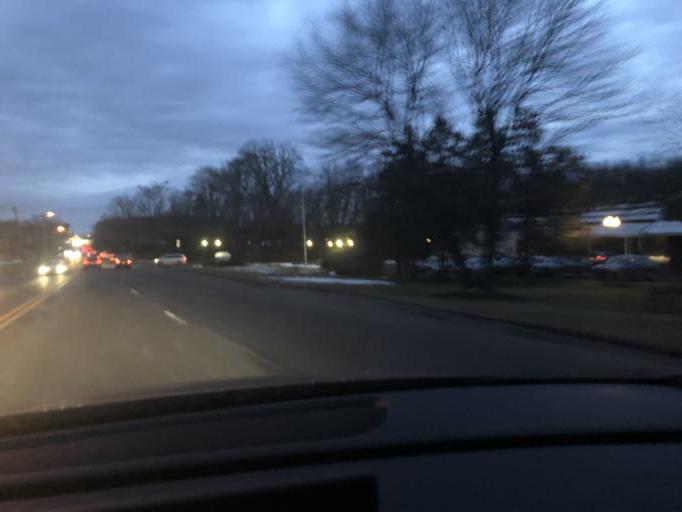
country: US
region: New Jersey
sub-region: Morris County
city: Florham Park
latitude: 40.7899
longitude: -74.4057
